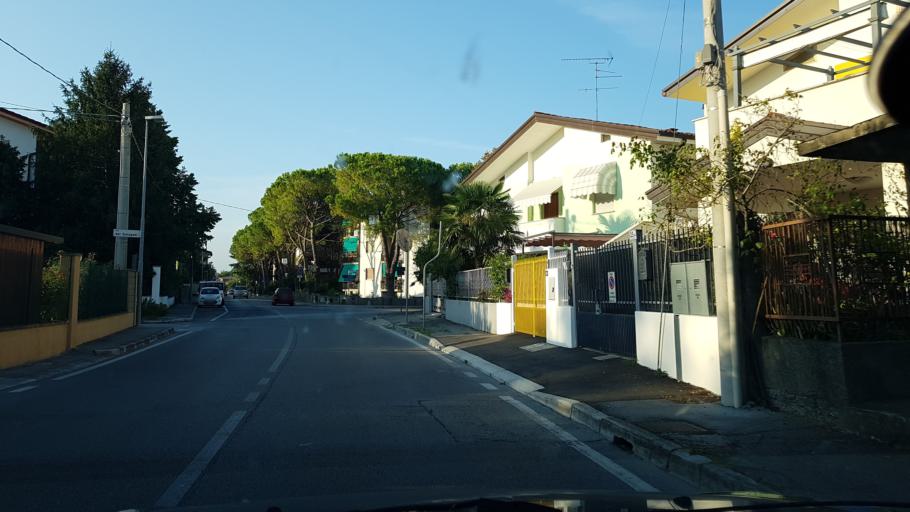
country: IT
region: Friuli Venezia Giulia
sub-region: Provincia di Gorizia
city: Staranzano
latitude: 45.7978
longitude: 13.5064
